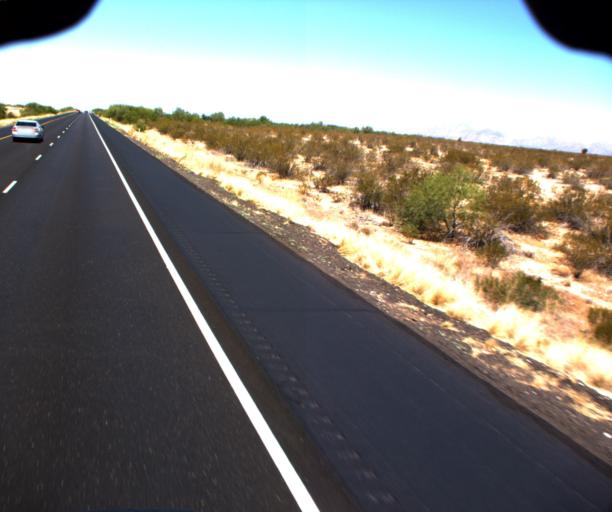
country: US
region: Arizona
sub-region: Yavapai County
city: Congress
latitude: 34.0615
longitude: -112.8615
